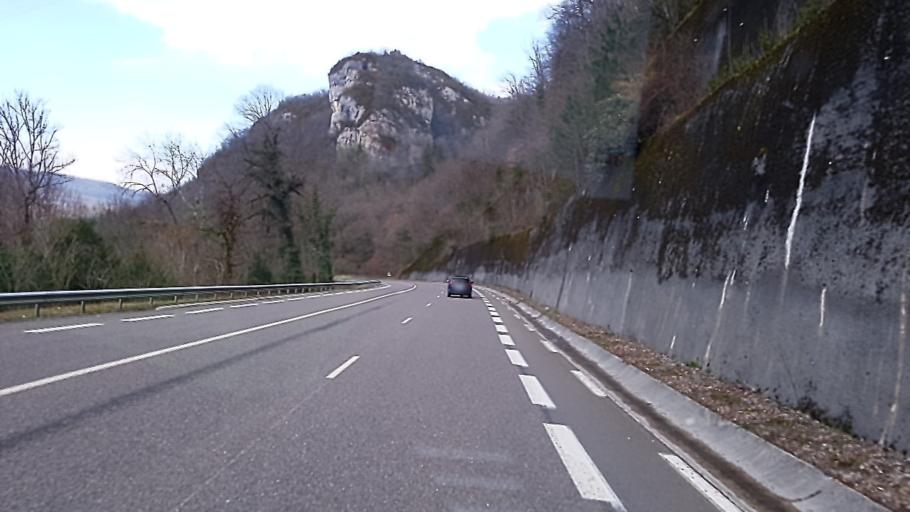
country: FR
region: Franche-Comte
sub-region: Departement du Jura
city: Lavans-les-Saint-Claude
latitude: 46.3723
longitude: 5.8012
